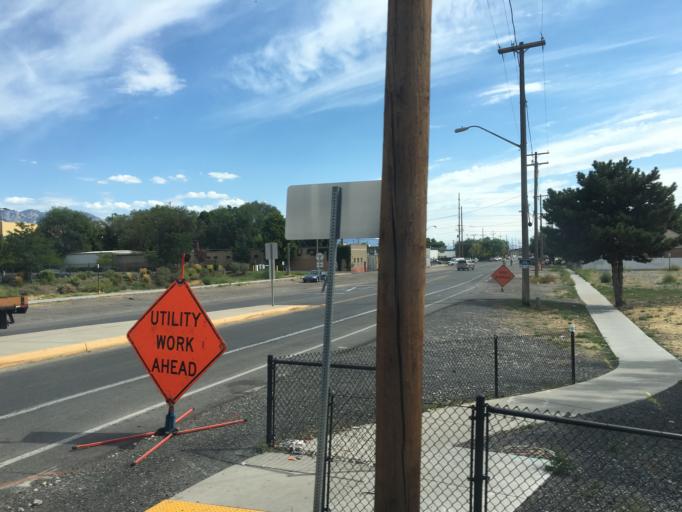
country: US
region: Utah
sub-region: Salt Lake County
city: Salt Lake City
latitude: 40.7692
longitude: -111.9083
